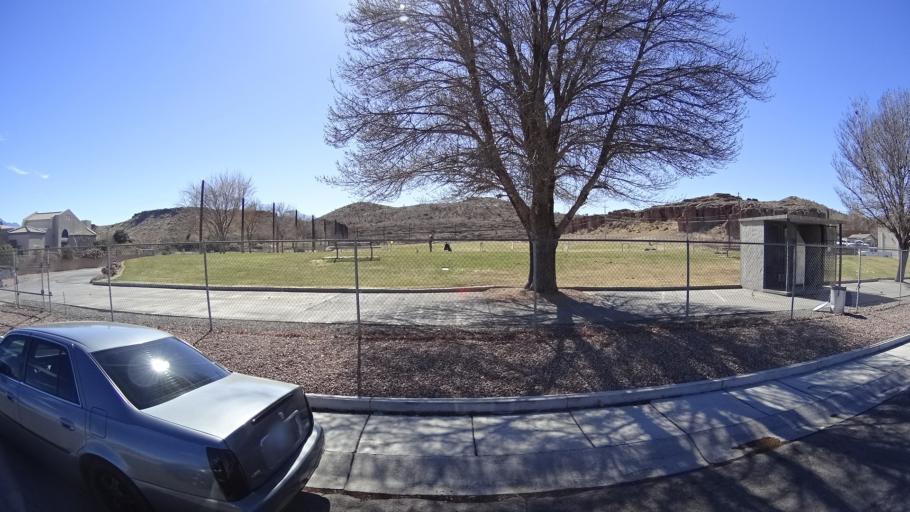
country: US
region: Arizona
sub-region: Mohave County
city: Kingman
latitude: 35.2061
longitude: -114.0429
